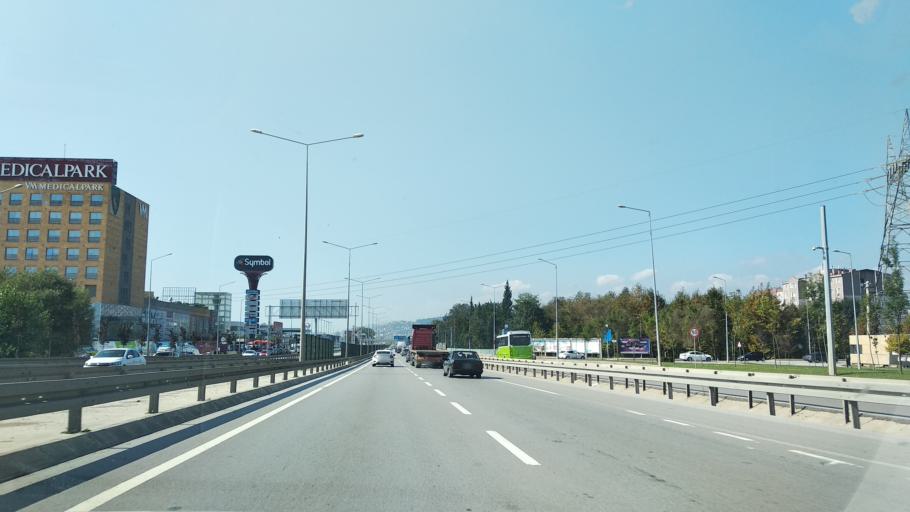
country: TR
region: Kocaeli
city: Kullar
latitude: 40.7593
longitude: 29.9826
